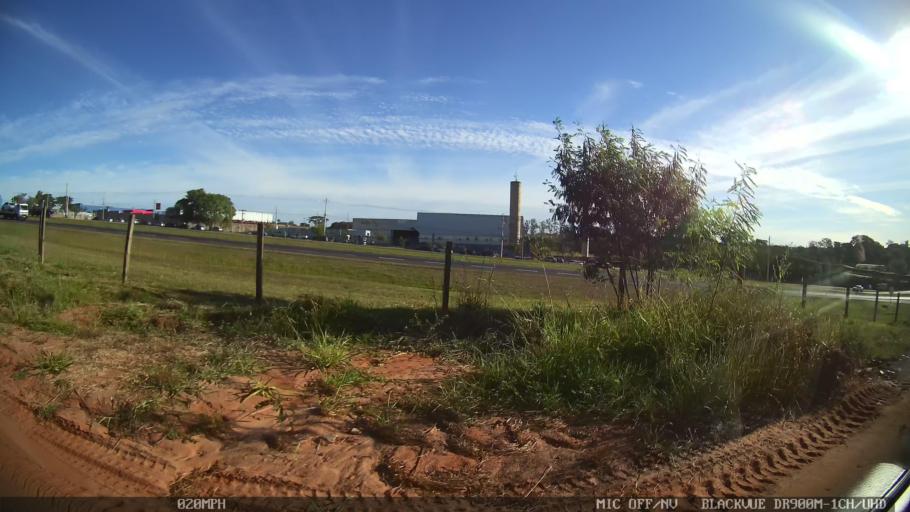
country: BR
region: Sao Paulo
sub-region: Sao Jose Do Rio Preto
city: Sao Jose do Rio Preto
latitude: -20.8730
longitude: -49.3233
